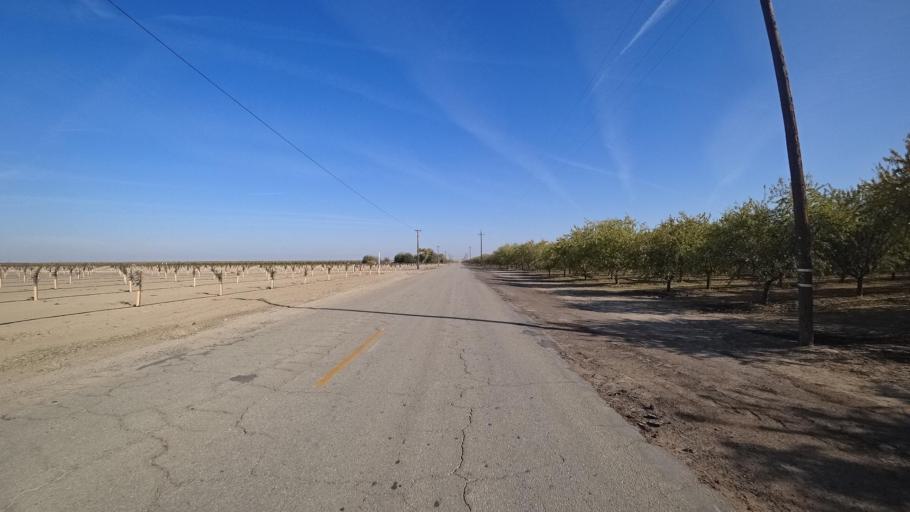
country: US
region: California
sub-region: Kern County
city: Wasco
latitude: 35.7036
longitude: -119.3626
